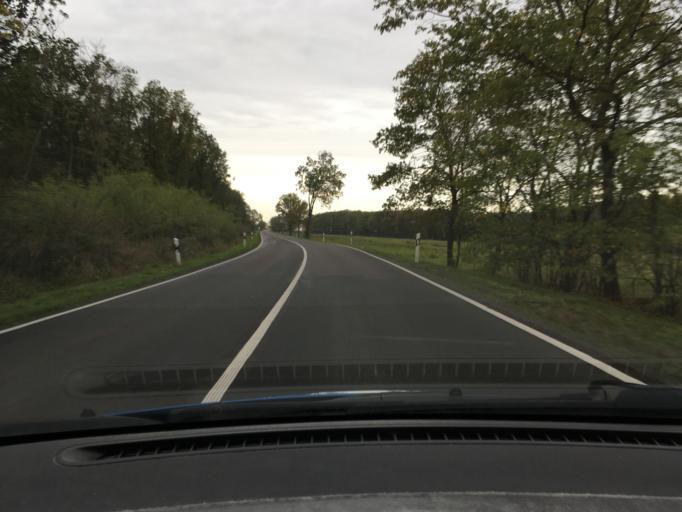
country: DE
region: Saxony-Anhalt
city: Leitzkau
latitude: 52.0333
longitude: 11.9922
